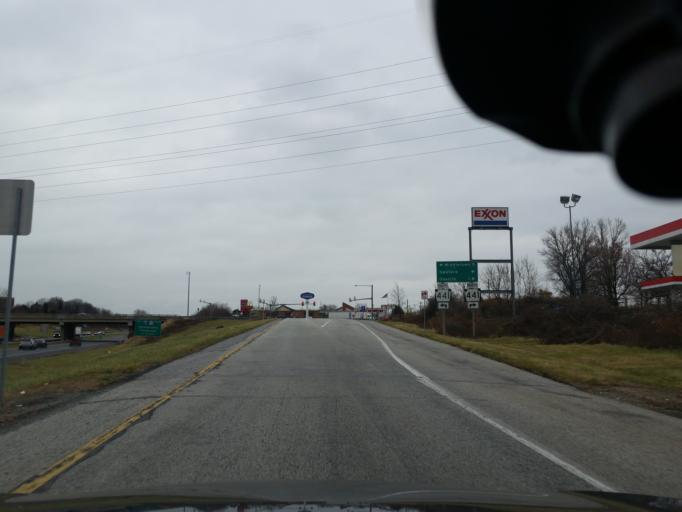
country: US
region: Pennsylvania
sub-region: Dauphin County
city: Lawnton
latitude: 40.2437
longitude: -76.8073
